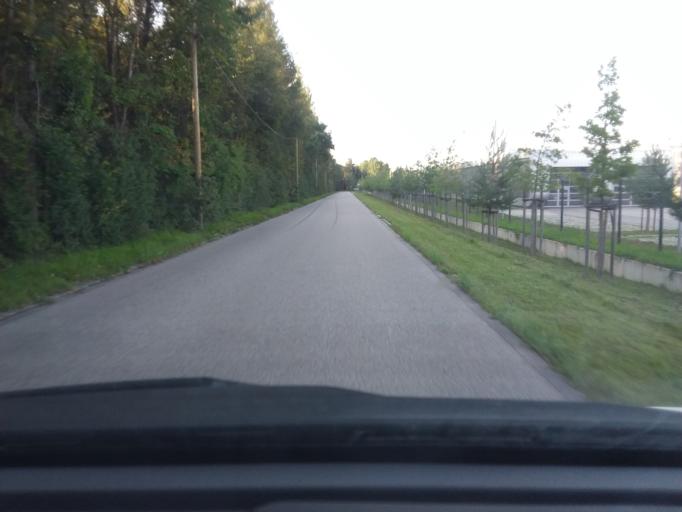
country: DE
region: Bavaria
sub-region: Upper Bavaria
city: Oberschleissheim
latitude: 48.2298
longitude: 11.5637
